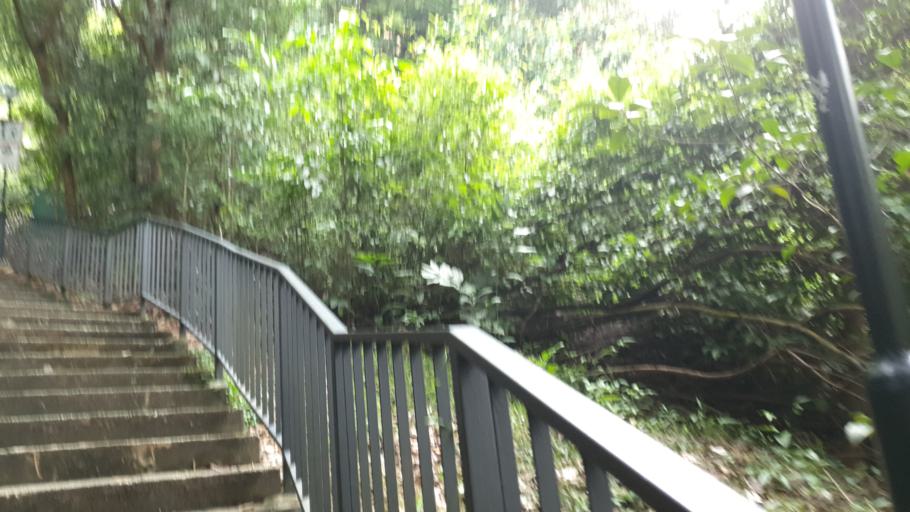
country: SG
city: Singapore
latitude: 1.2740
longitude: 103.8189
